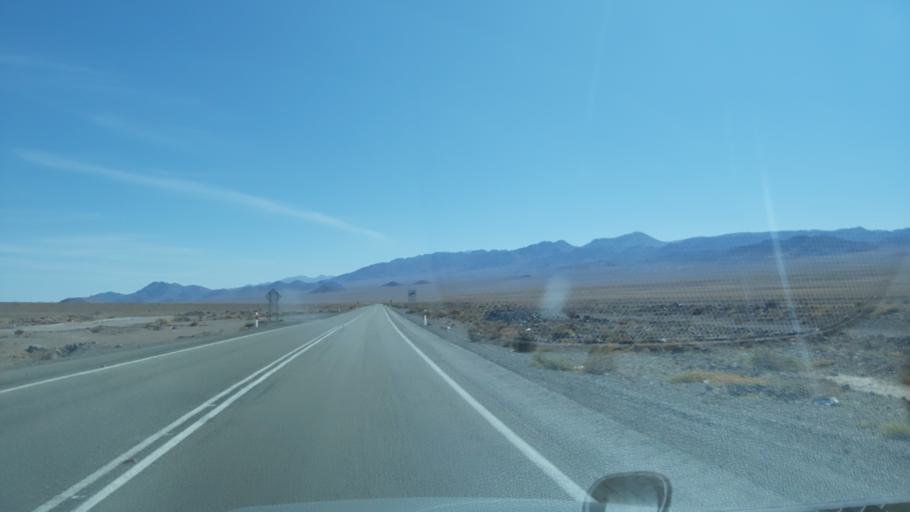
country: CL
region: Atacama
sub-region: Provincia de Chanaral
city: Diego de Almagro
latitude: -26.8582
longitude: -69.9019
